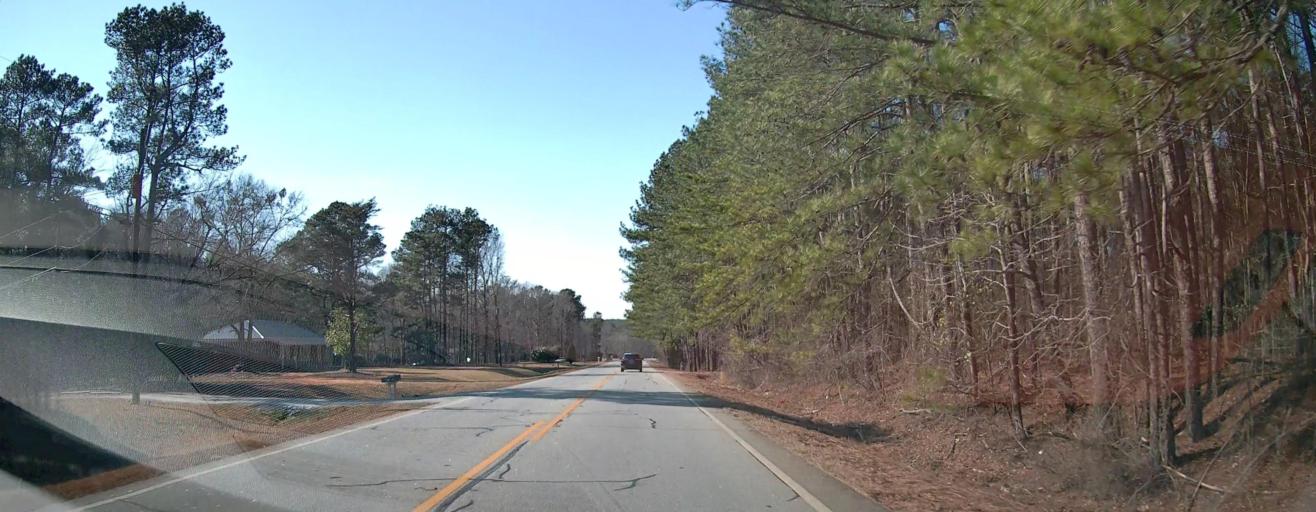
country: US
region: Georgia
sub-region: Butts County
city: Indian Springs
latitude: 33.2498
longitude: -83.8925
